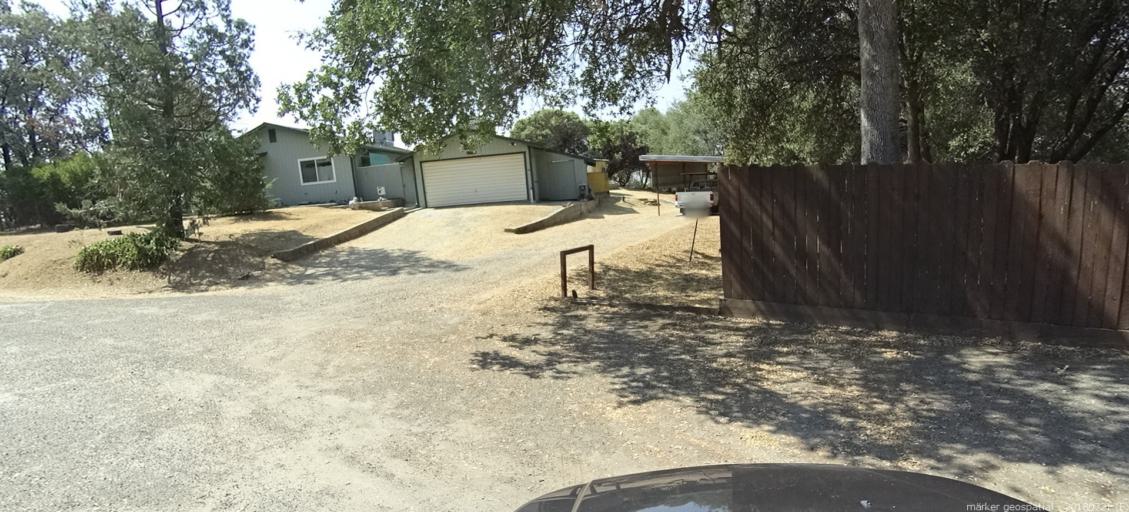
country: US
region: California
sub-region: Fresno County
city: Auberry
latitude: 37.2153
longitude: -119.5218
